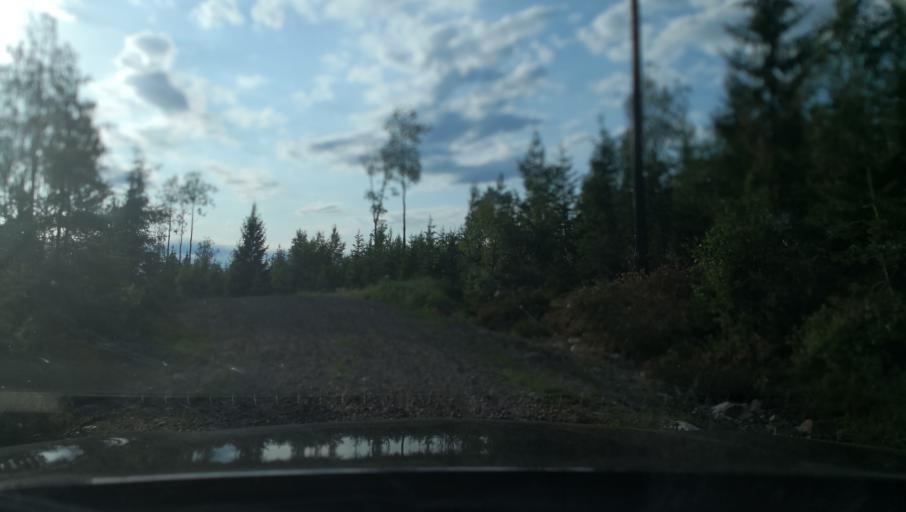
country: SE
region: Dalarna
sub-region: Smedjebackens Kommun
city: Smedjebacken
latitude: 60.0688
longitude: 15.3051
